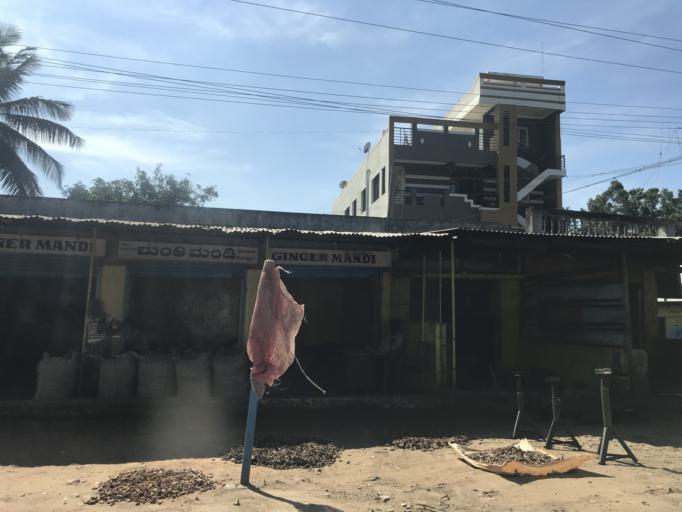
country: IN
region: Karnataka
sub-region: Mysore
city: Heggadadevankote
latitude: 12.0657
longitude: 76.3545
